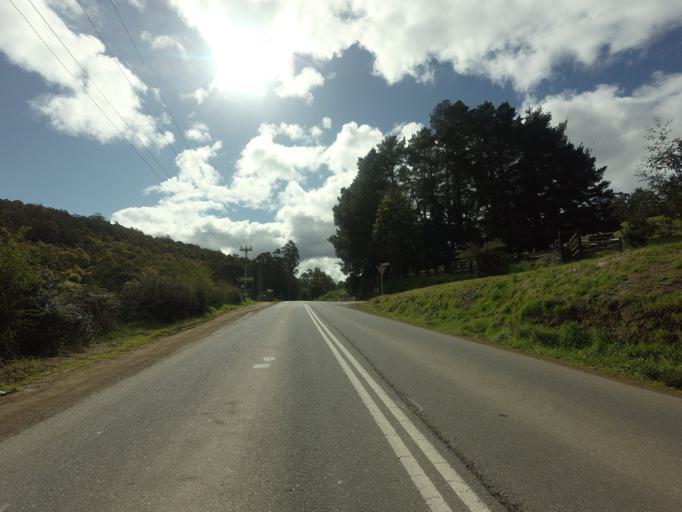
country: AU
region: Tasmania
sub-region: Huon Valley
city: Geeveston
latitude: -43.2375
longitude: 146.9909
